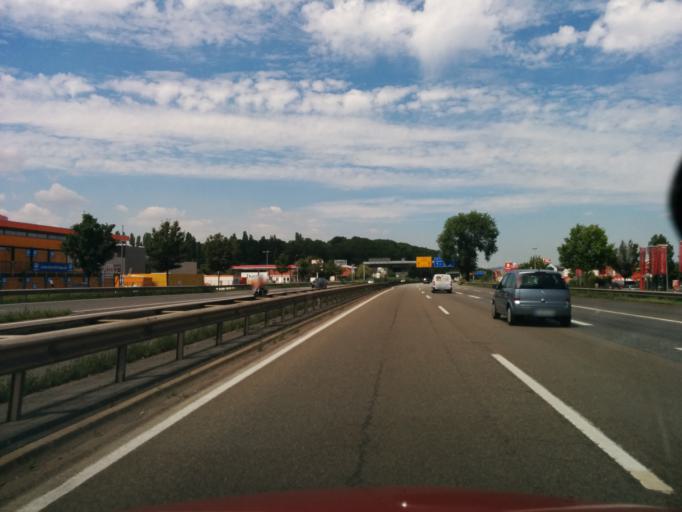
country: DE
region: Rheinland-Pfalz
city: Kaltenengers
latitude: 50.3867
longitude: 7.5574
